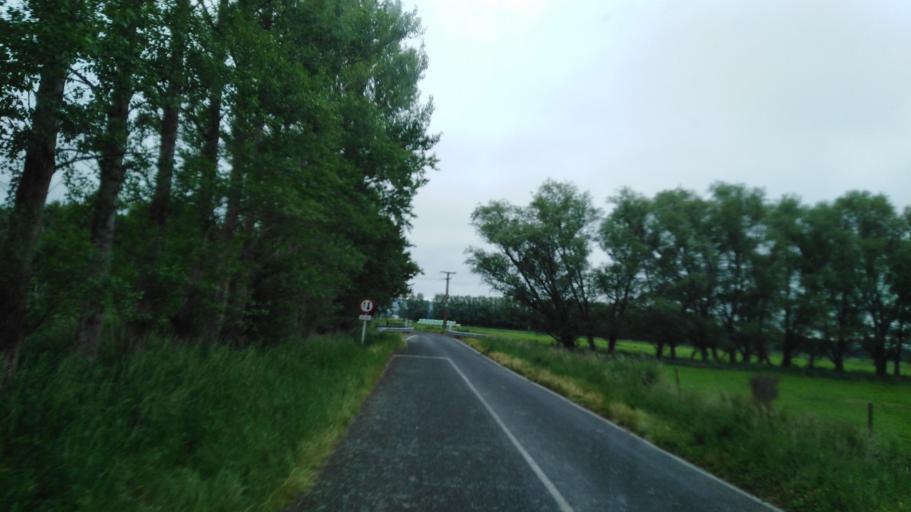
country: NZ
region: Bay of Plenty
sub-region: Rotorua District
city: Rotorua
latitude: -38.4143
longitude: 176.3386
